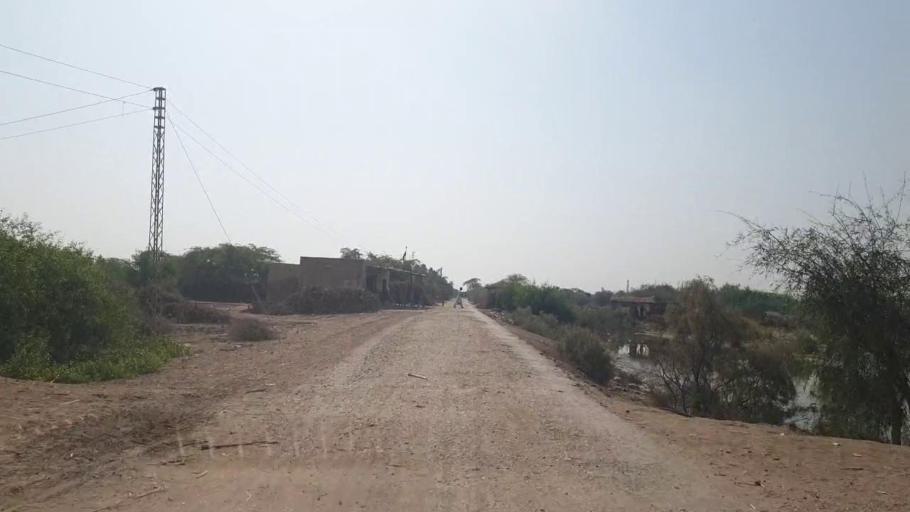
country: PK
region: Sindh
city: Berani
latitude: 25.8934
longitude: 68.7504
